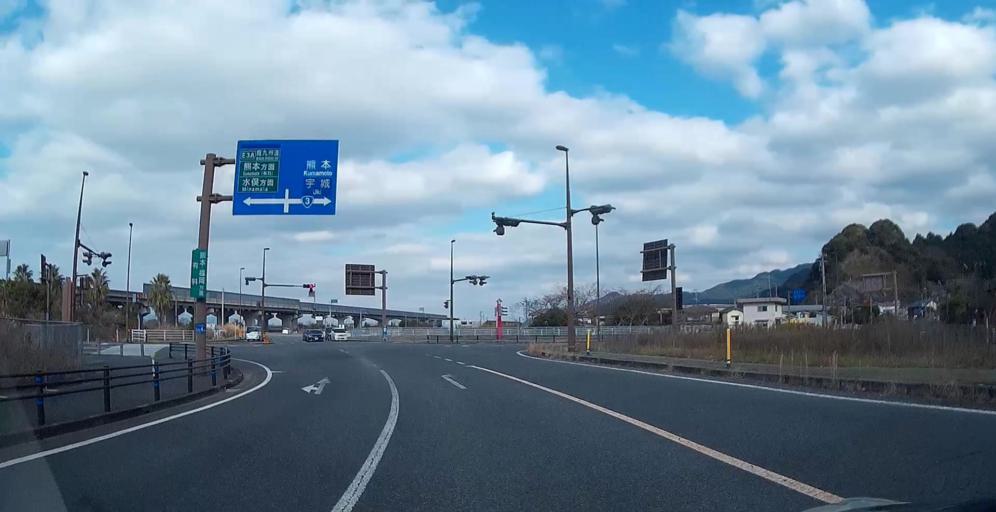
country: JP
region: Kumamoto
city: Yatsushiro
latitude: 32.4304
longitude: 130.5685
